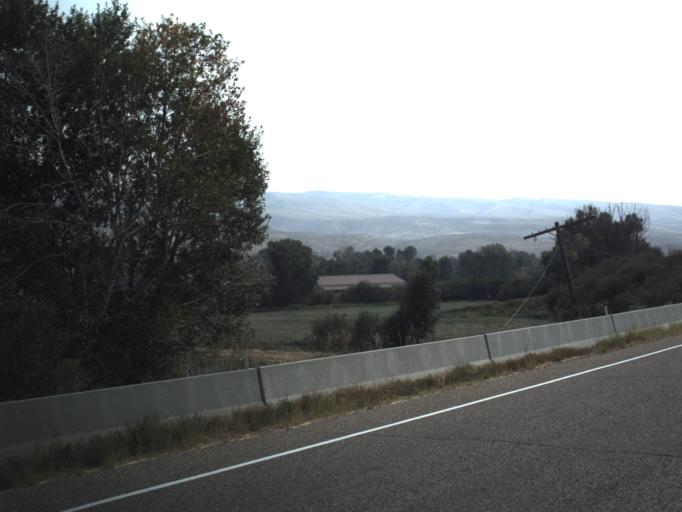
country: US
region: Utah
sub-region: Summit County
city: Coalville
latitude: 41.0292
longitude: -111.5091
